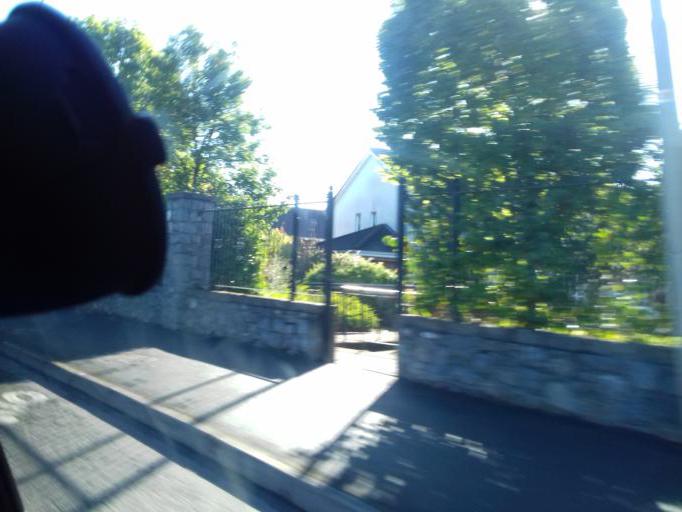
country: IE
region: Leinster
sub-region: Uibh Fhaili
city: Tullamore
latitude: 53.2881
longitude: -7.5050
